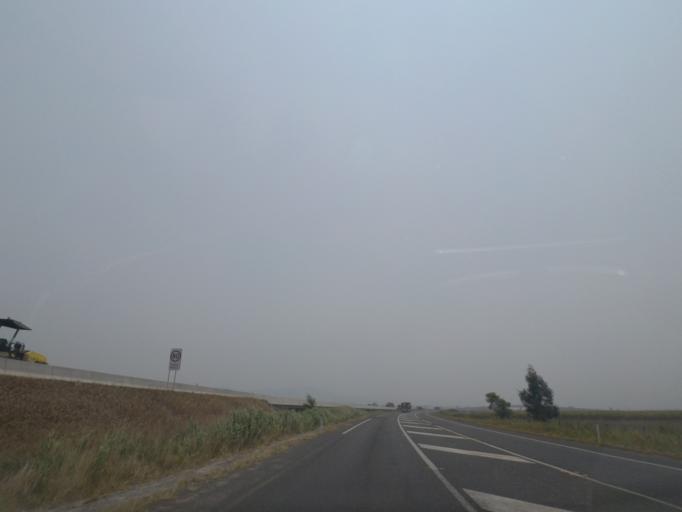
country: AU
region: New South Wales
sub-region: Clarence Valley
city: Maclean
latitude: -29.4002
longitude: 153.2406
